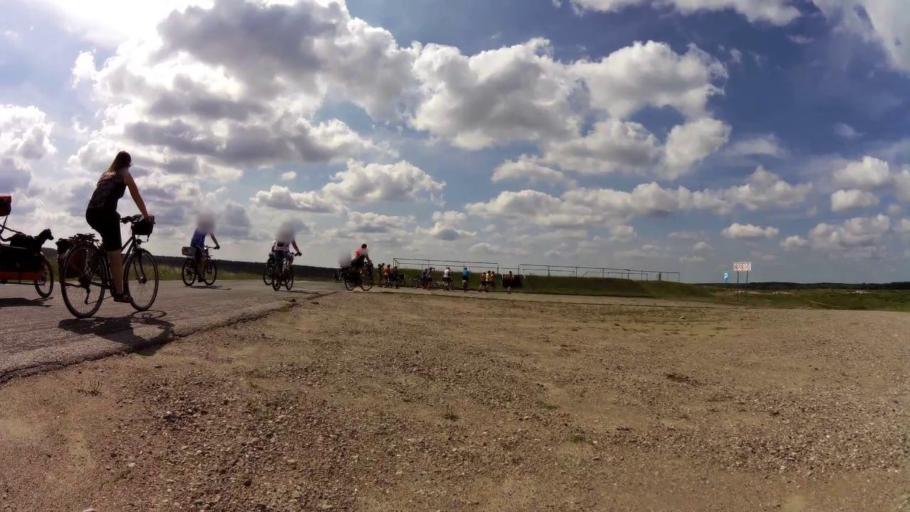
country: PL
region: West Pomeranian Voivodeship
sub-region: Powiat drawski
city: Drawsko Pomorskie
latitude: 53.4525
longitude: 15.7739
